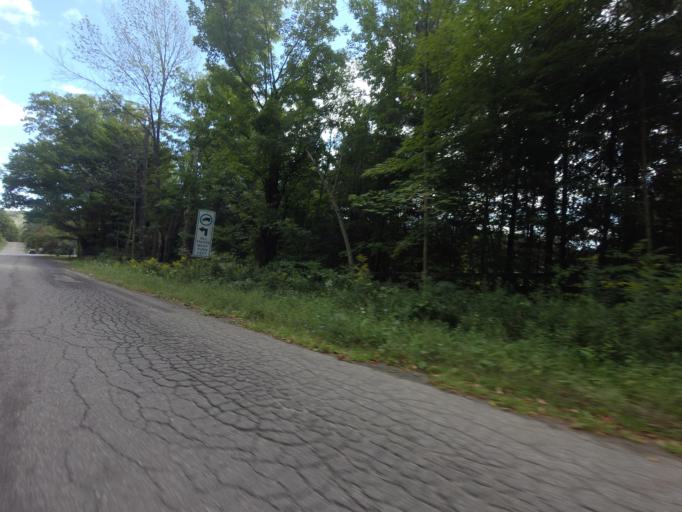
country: CA
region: Ontario
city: Orangeville
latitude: 43.8130
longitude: -79.9805
